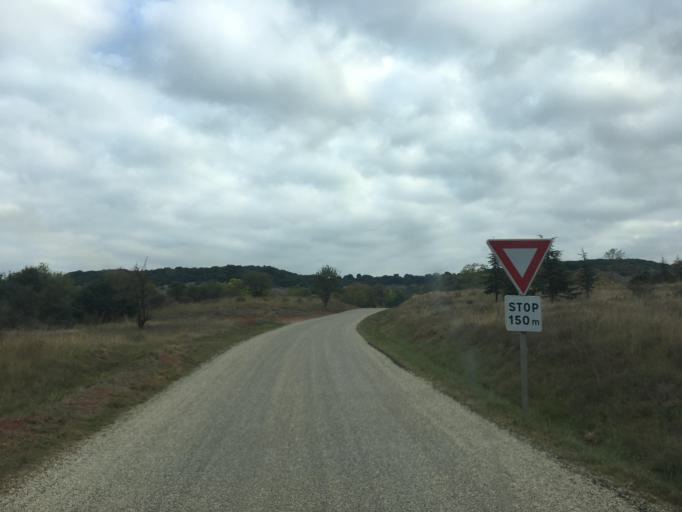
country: FR
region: Languedoc-Roussillon
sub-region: Departement de l'Herault
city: Nebian
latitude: 43.6433
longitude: 3.3894
